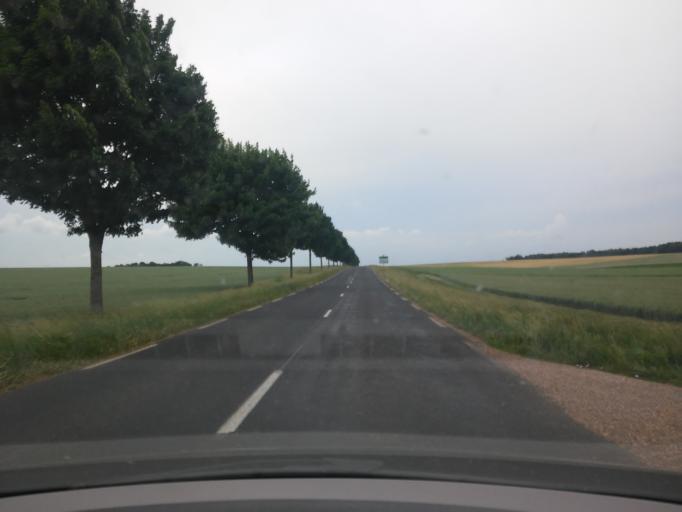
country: FR
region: Lorraine
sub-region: Departement de Meurthe-et-Moselle
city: Montauville
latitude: 48.8847
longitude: 5.8878
